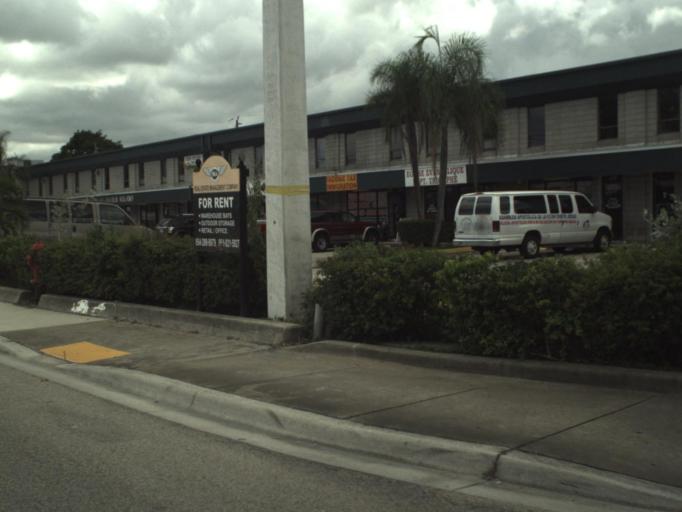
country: US
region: Florida
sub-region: Broward County
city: Kendall Green
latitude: 26.2570
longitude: -80.1190
